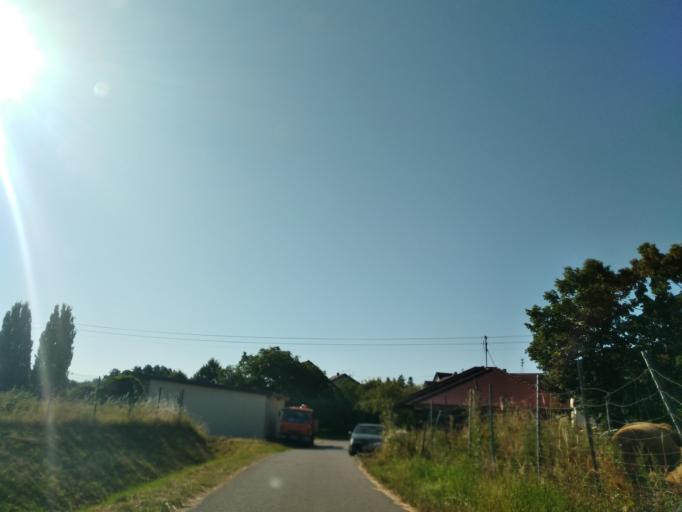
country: DE
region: Baden-Wuerttemberg
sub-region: Karlsruhe Region
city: Limbach
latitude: 49.4807
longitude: 9.2128
